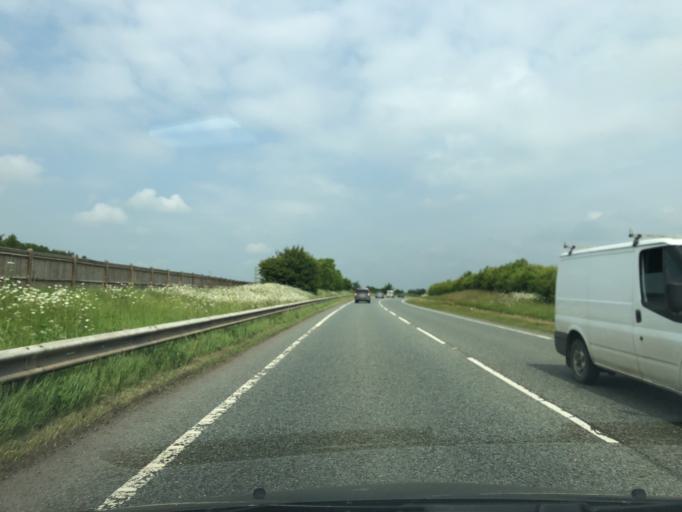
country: GB
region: England
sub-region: North Yorkshire
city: Boroughbridge
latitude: 54.1467
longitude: -1.4322
